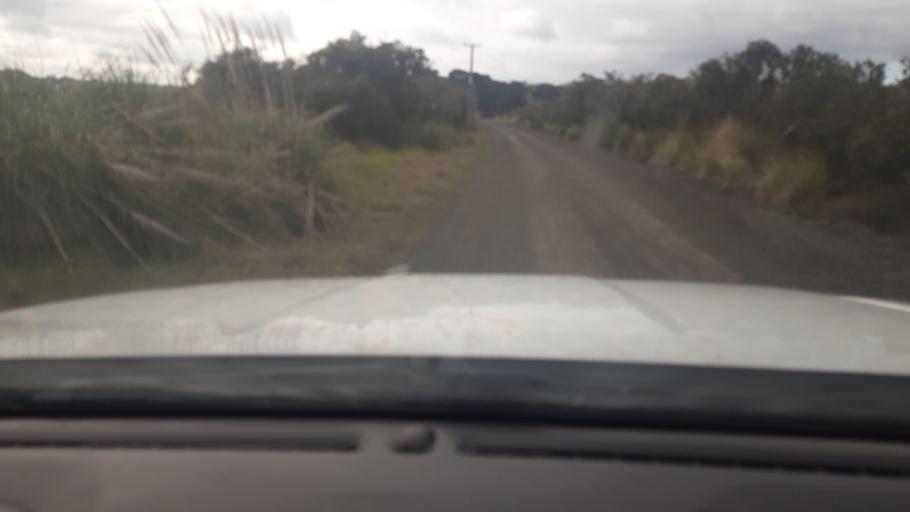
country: NZ
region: Northland
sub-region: Far North District
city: Ahipara
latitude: -35.2578
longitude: 173.2070
